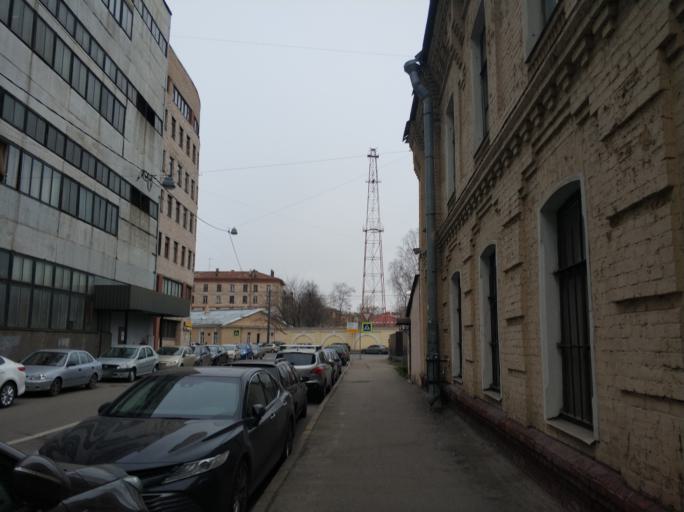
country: RU
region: St.-Petersburg
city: Petrogradka
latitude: 59.9649
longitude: 30.3317
